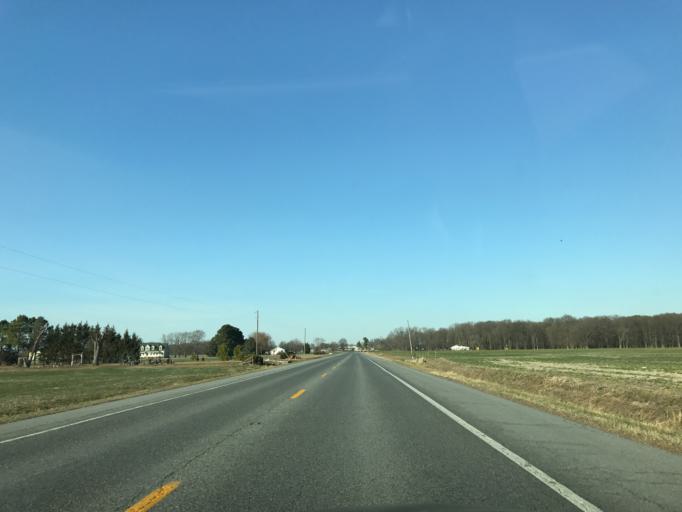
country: US
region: Maryland
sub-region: Caroline County
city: Greensboro
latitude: 39.1300
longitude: -75.8656
